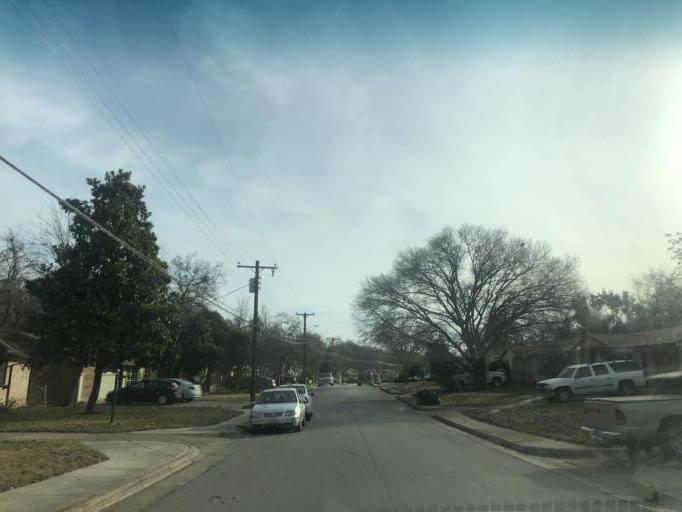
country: US
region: Texas
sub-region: Dallas County
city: Duncanville
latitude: 32.6707
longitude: -96.8963
